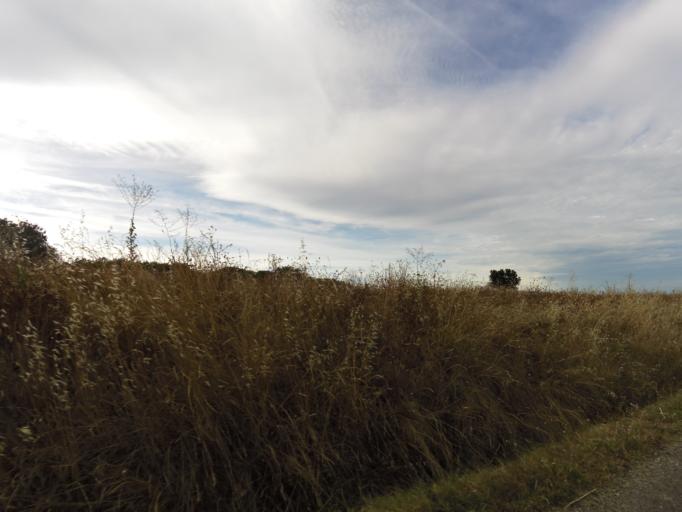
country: FR
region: Languedoc-Roussillon
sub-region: Departement du Gard
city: Saint-Genies-de-Malgoires
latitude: 43.9248
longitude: 4.2037
